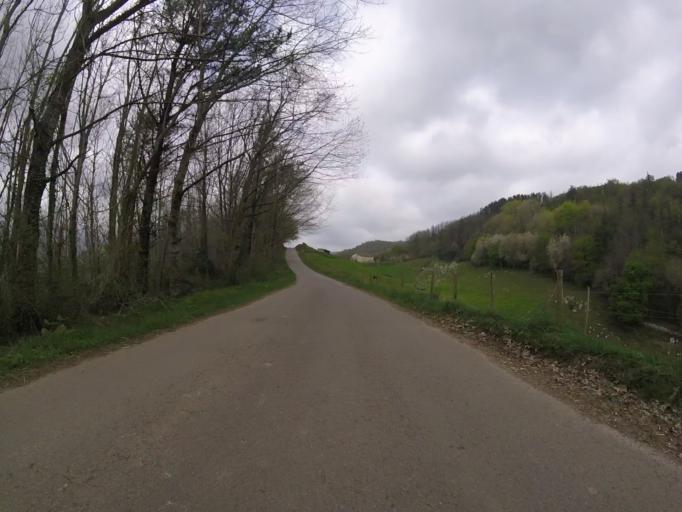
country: ES
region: Basque Country
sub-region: Provincia de Guipuzcoa
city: Zizurkil
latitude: 43.2097
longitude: -2.0784
